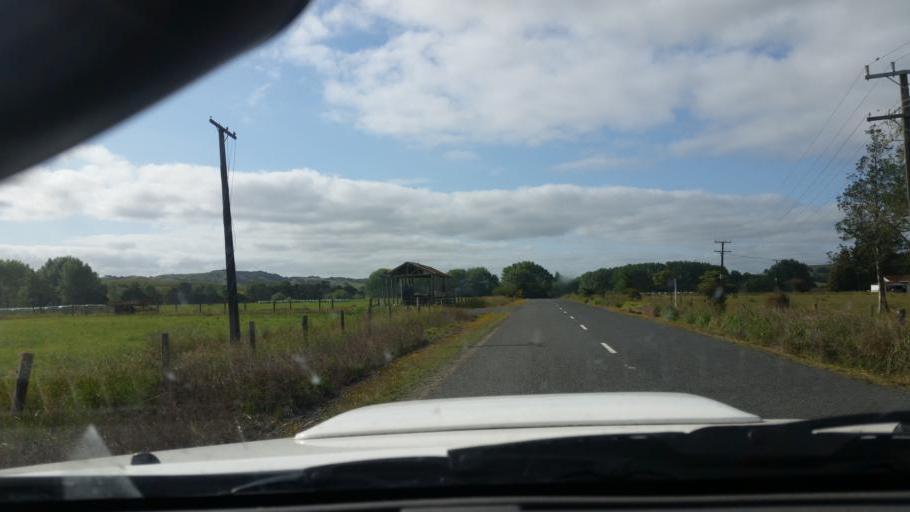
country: NZ
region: Northland
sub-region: Kaipara District
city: Dargaville
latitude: -35.8360
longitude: 173.8433
